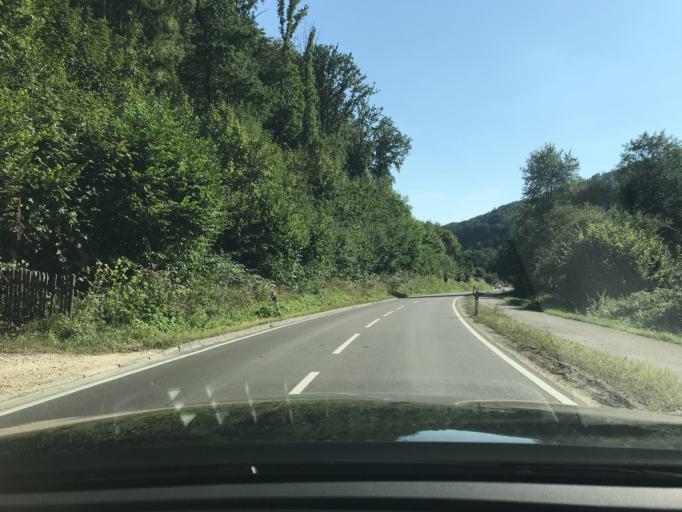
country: DE
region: Baden-Wuerttemberg
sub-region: Regierungsbezirk Stuttgart
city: Reichenbach an der Fils
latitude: 48.7248
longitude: 9.4654
